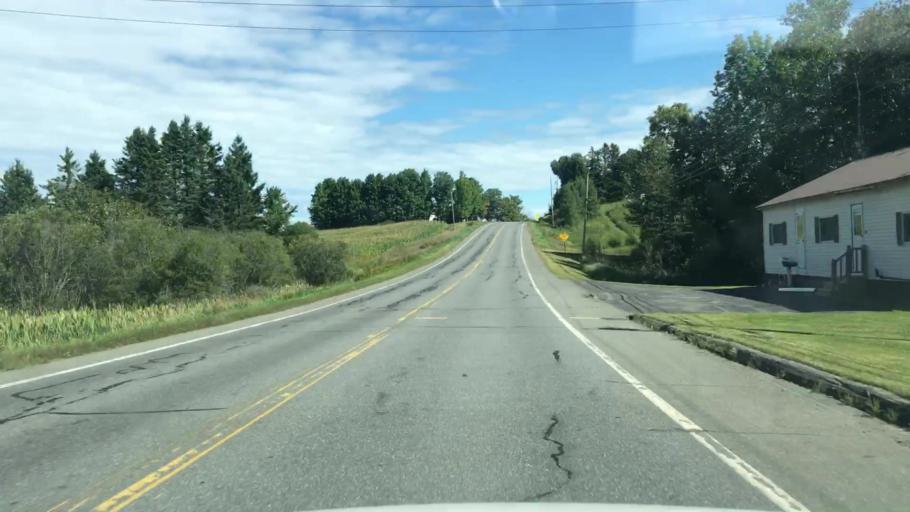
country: US
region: Maine
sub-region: Penobscot County
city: Dexter
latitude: 45.0727
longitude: -69.2360
